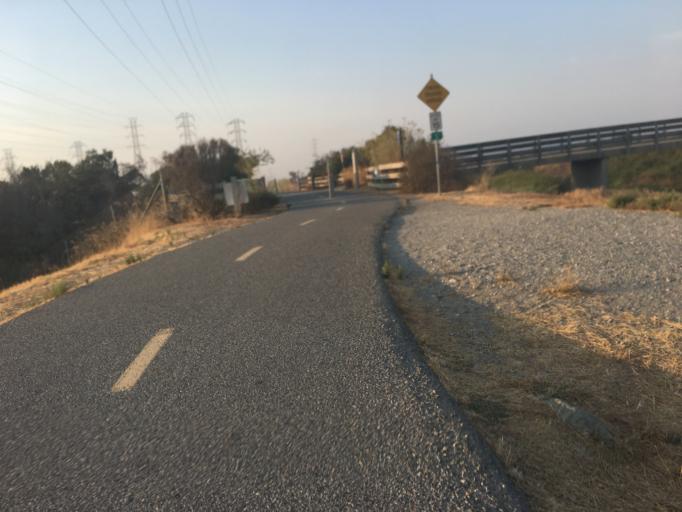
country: US
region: California
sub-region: Santa Clara County
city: Mountain View
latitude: 37.4244
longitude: -122.0689
